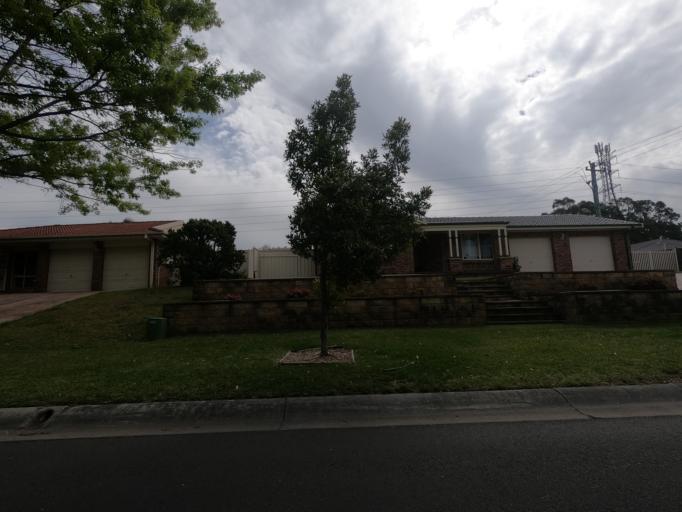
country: AU
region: New South Wales
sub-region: Wollongong
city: Dapto
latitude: -34.4905
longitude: 150.7723
